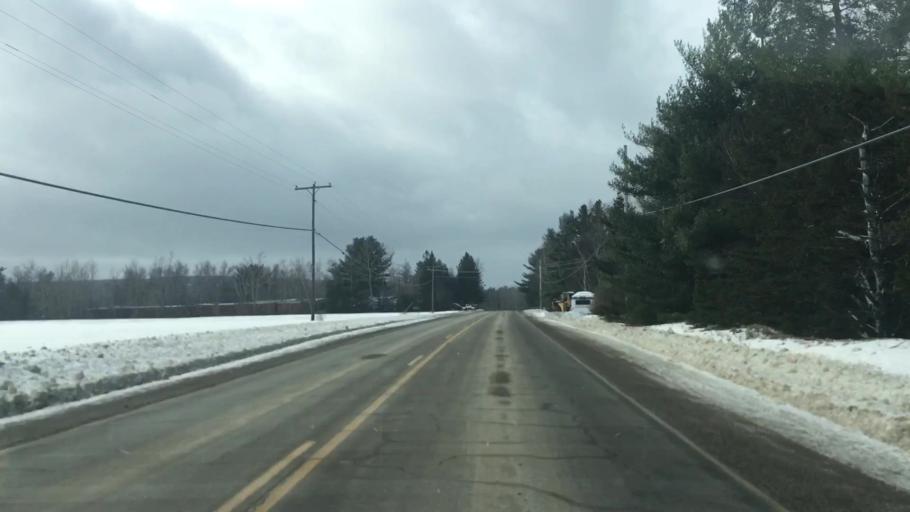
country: US
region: Maine
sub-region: Washington County
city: Calais
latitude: 45.0190
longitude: -67.3829
